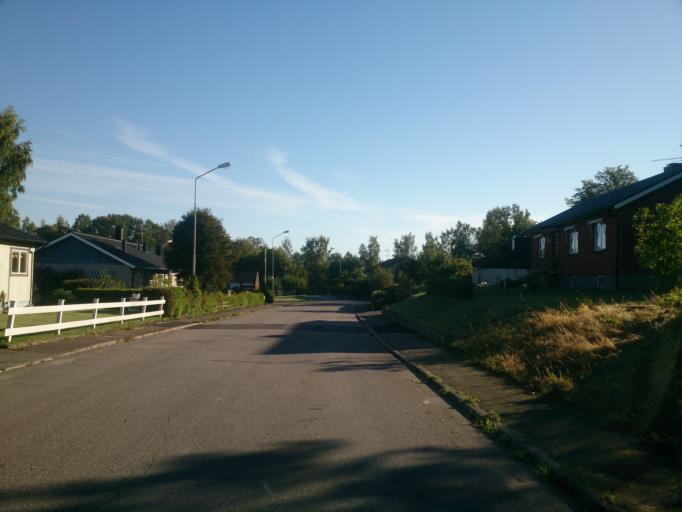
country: SE
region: OEstergoetland
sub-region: Atvidabergs Kommun
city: Atvidaberg
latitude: 58.1877
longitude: 16.0160
